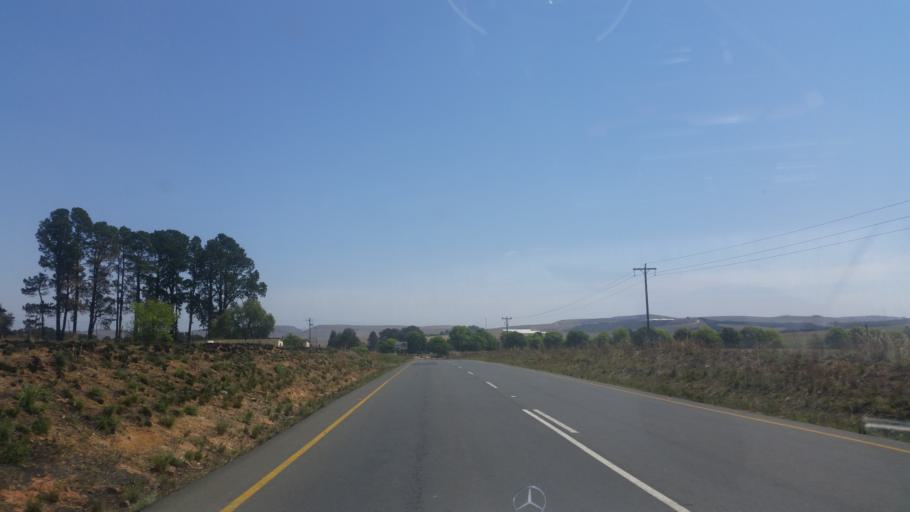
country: ZA
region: KwaZulu-Natal
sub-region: uMgungundlovu District Municipality
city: Mooirivier
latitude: -29.1489
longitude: 29.9799
